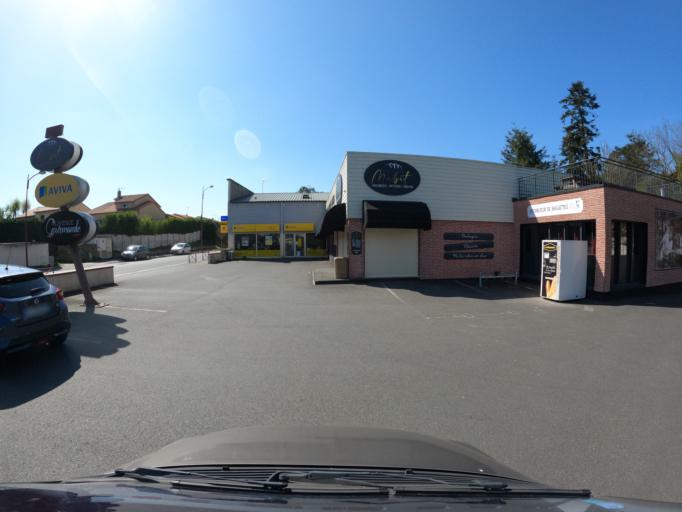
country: FR
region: Pays de la Loire
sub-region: Departement de Maine-et-Loire
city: La Seguiniere
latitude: 47.0601
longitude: -0.9377
